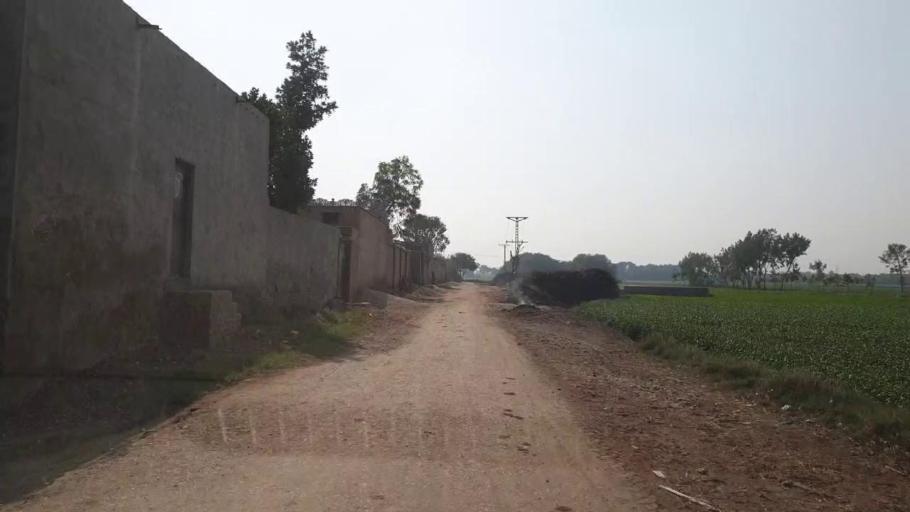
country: PK
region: Sindh
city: Bhit Shah
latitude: 25.7499
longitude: 68.5166
